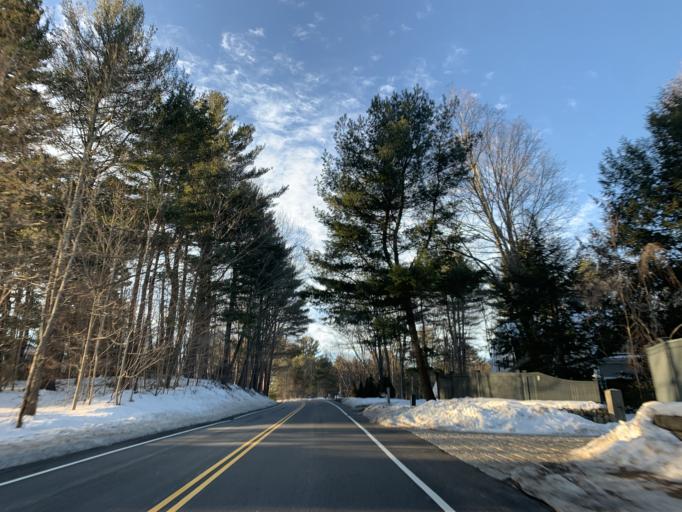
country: US
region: Massachusetts
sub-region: Norfolk County
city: Westwood
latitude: 42.2464
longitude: -71.2218
